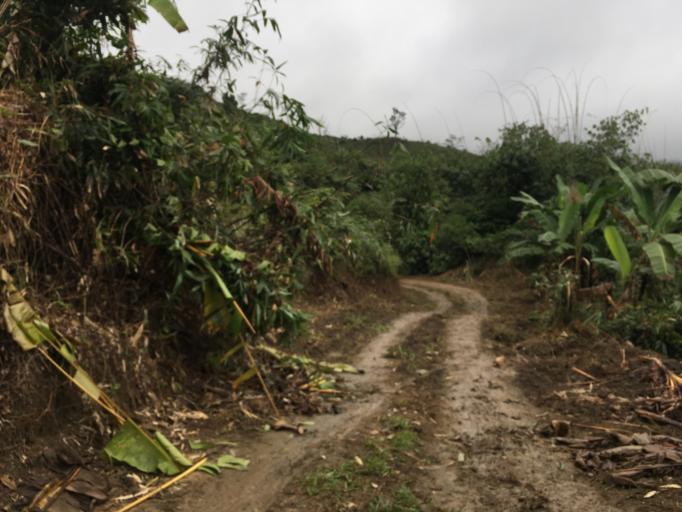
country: LA
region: Houaphan
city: Xamtay
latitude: 19.9032
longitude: 104.4591
